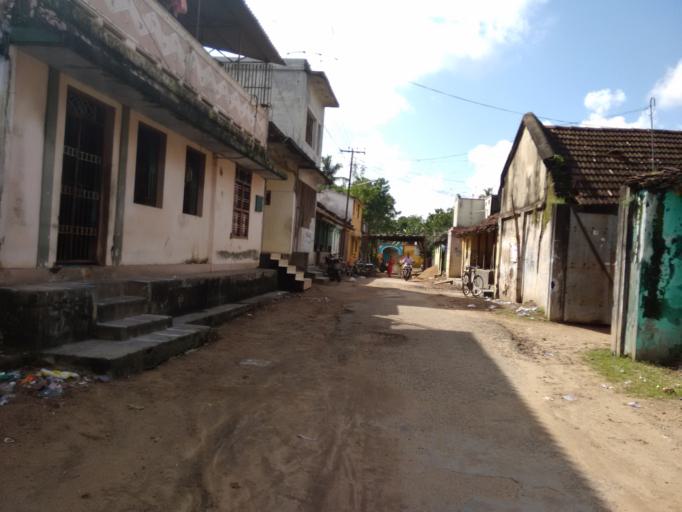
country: IN
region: Tamil Nadu
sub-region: Thiruvarur
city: Koradachcheri
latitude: 10.8492
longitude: 79.5128
